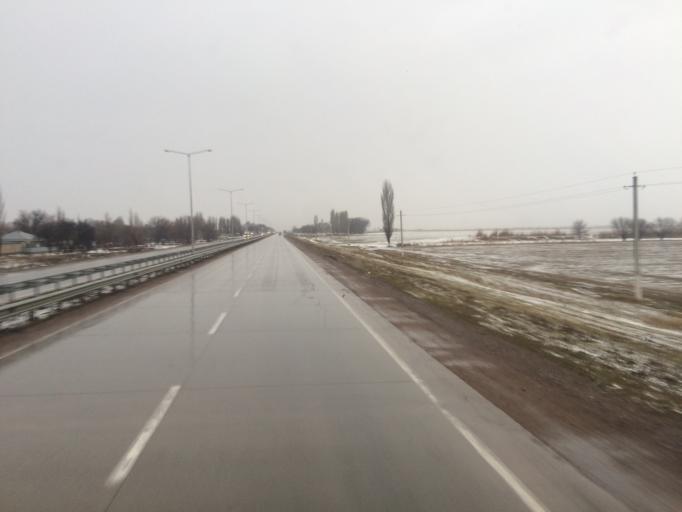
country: KZ
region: Zhambyl
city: Merke
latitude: 42.8771
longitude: 73.1076
